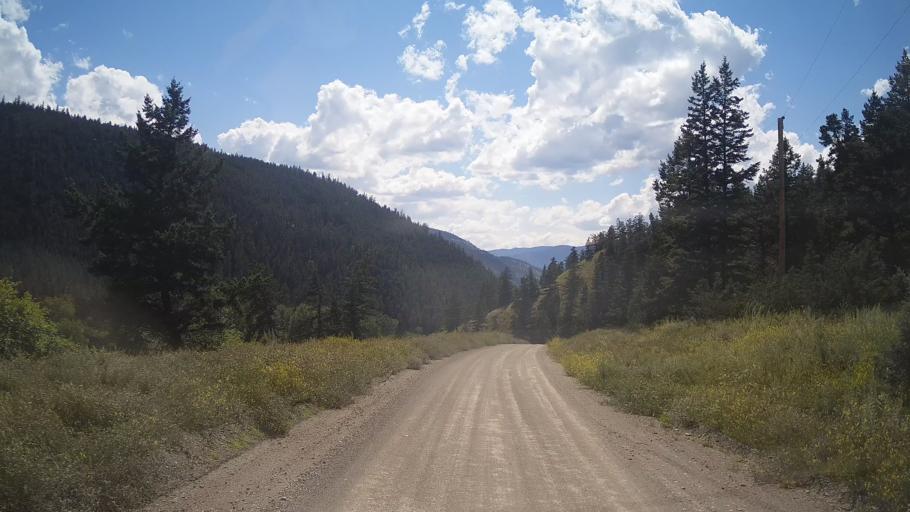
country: CA
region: British Columbia
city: Lillooet
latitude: 51.2500
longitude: -122.0245
